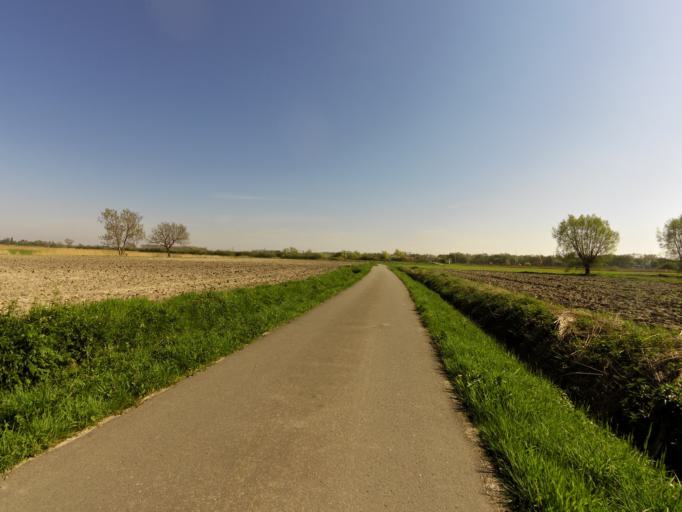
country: BE
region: Flanders
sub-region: Provincie West-Vlaanderen
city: Jabbeke
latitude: 51.2002
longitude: 3.0659
